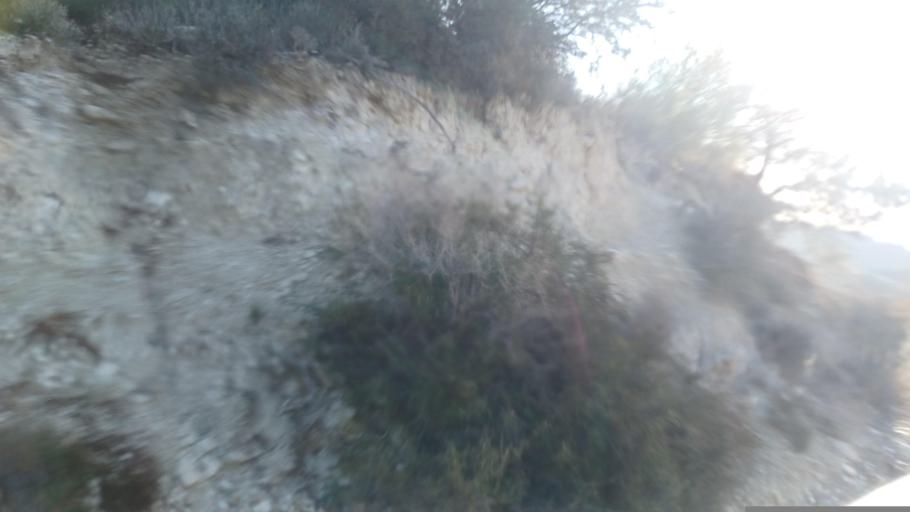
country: CY
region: Larnaka
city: Kofinou
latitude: 34.8238
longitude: 33.3101
